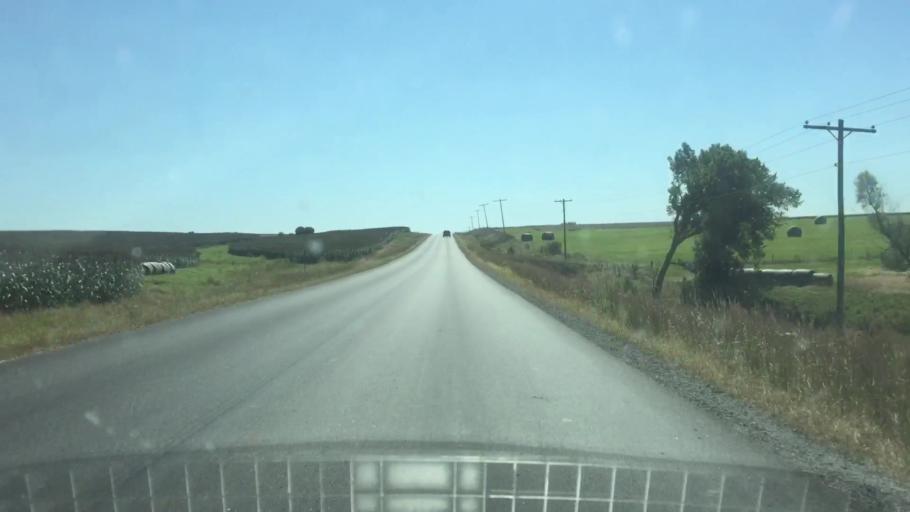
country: US
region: Kansas
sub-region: Marshall County
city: Marysville
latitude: 39.8961
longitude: -96.6010
